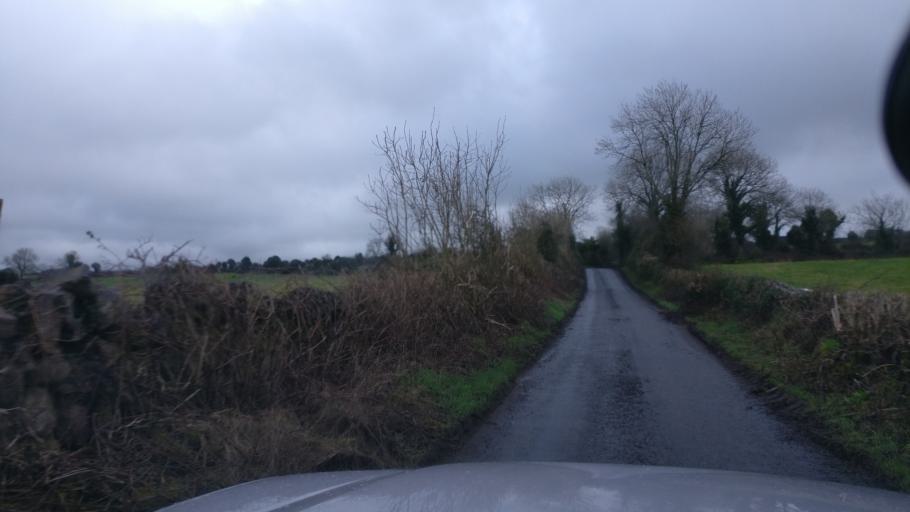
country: IE
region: Connaught
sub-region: County Galway
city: Athenry
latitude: 53.2104
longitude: -8.6920
